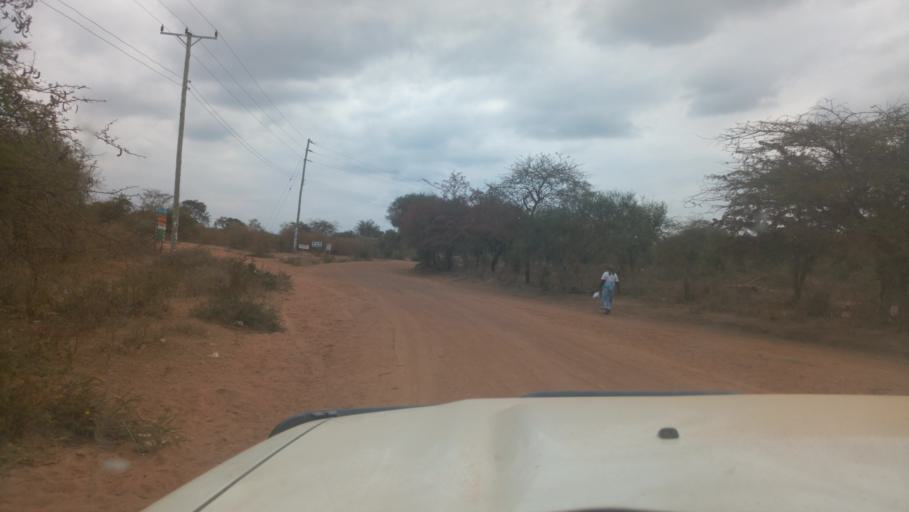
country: KE
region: Kitui
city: Kitui
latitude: -1.6000
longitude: 37.8759
